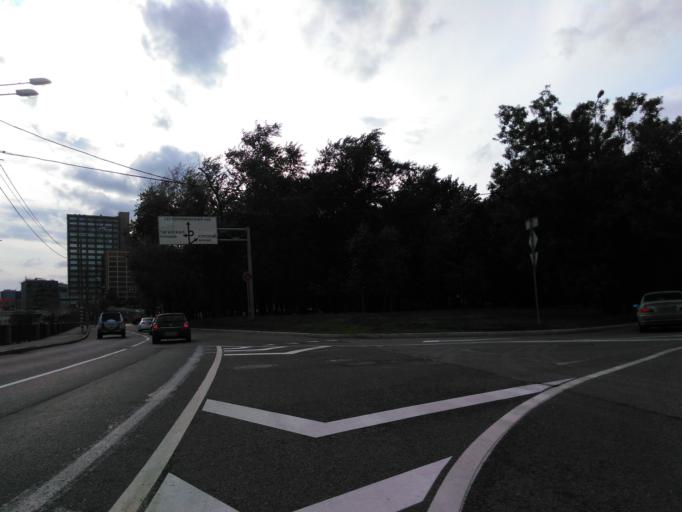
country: RU
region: Moscow
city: Taganskiy
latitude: 55.7503
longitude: 37.6624
